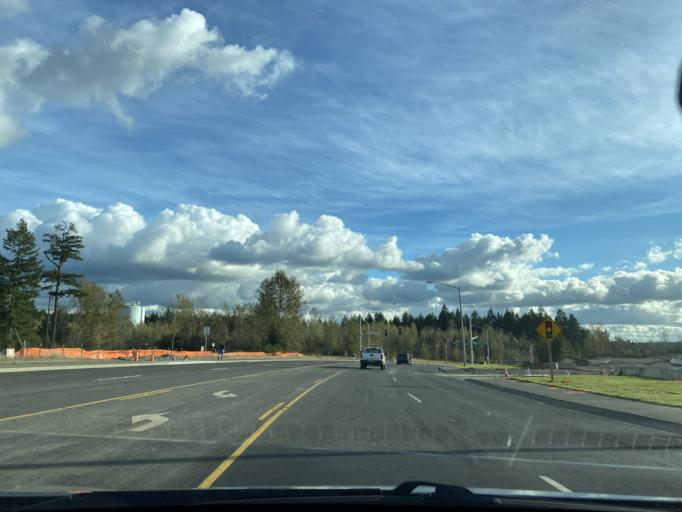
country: US
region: Washington
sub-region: Pierce County
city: South Hill
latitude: 47.0963
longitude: -122.2645
